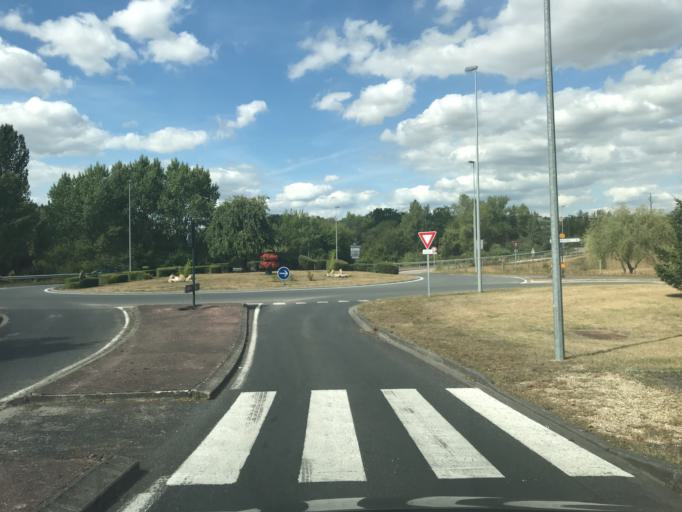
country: FR
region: Haute-Normandie
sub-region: Departement de l'Eure
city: Les Andelys
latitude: 49.2331
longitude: 1.3860
